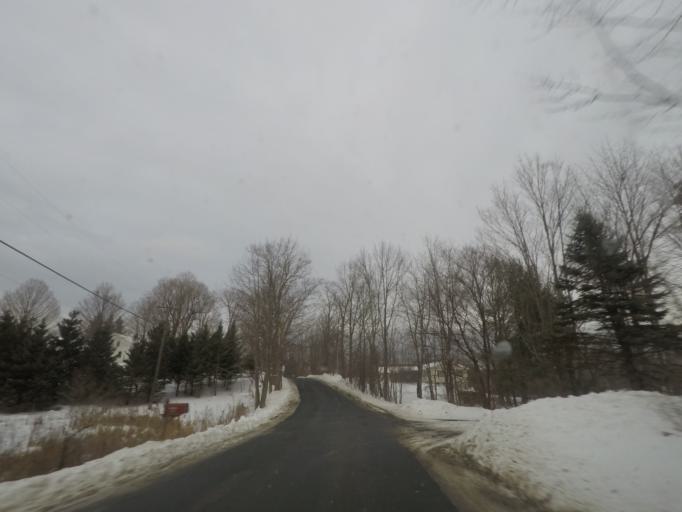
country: US
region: New York
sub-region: Rensselaer County
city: Averill Park
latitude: 42.5790
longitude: -73.5785
